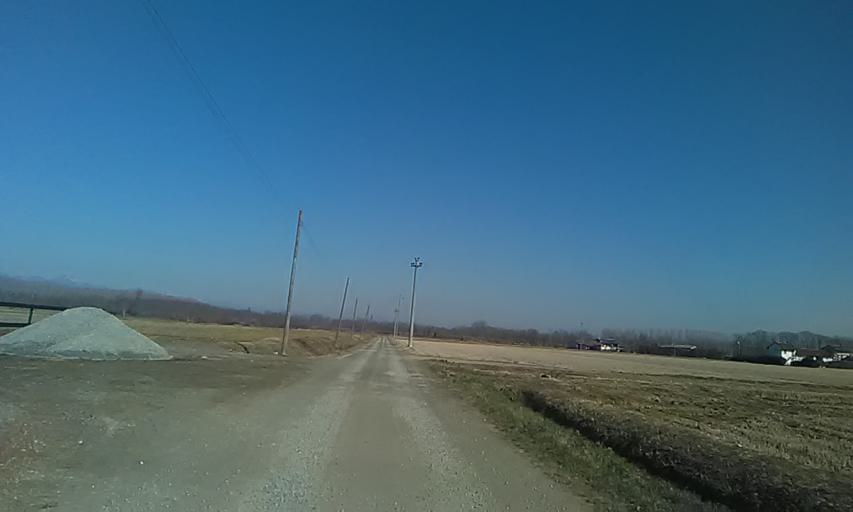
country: IT
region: Piedmont
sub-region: Provincia di Vercelli
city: Carisio
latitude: 45.4052
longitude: 8.2178
